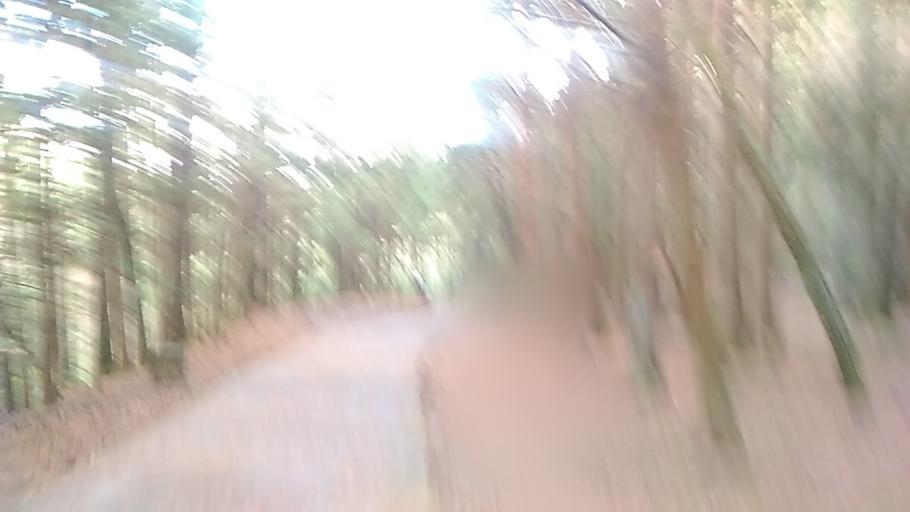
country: TW
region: Taiwan
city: Daxi
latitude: 24.4026
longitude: 121.3071
